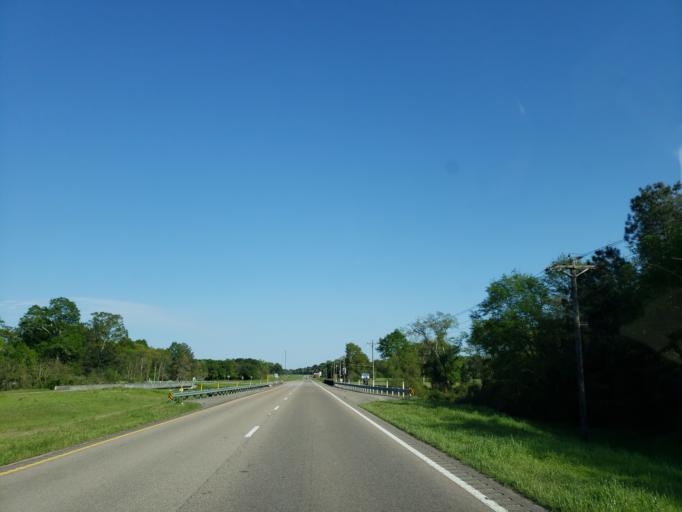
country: US
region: Mississippi
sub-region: Jones County
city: Ellisville
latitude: 31.6812
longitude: -89.3093
